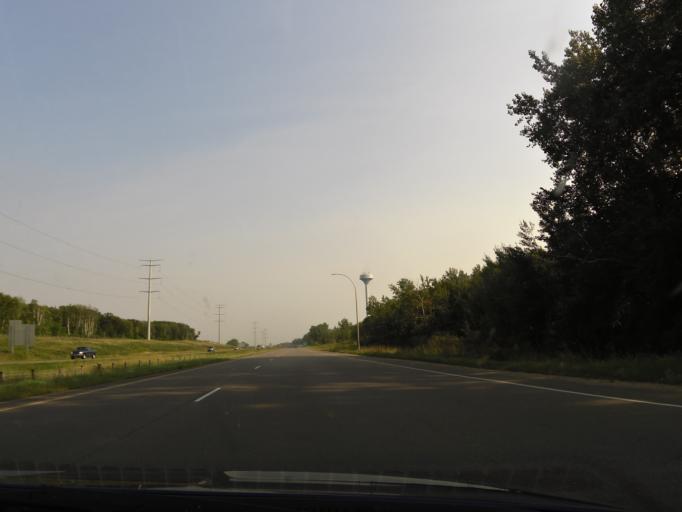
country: US
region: Minnesota
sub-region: Stearns County
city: Saint Joseph
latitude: 45.5112
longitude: -94.2796
